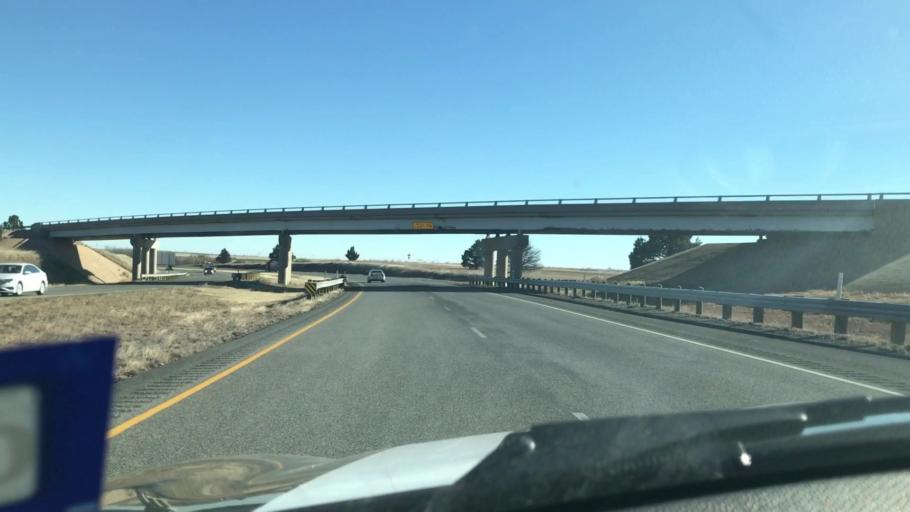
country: US
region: Texas
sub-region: Scurry County
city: Snyder
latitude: 32.6917
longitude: -100.8595
